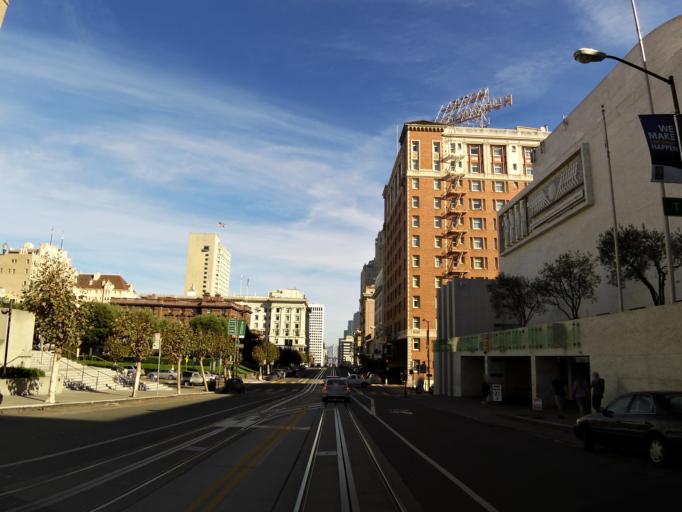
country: US
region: California
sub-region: San Francisco County
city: San Francisco
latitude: 37.7915
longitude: -122.4134
